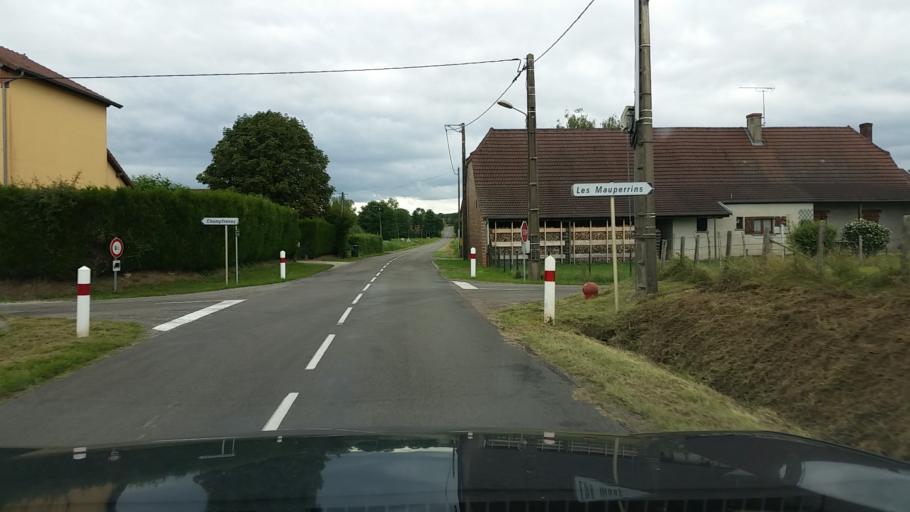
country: FR
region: Bourgogne
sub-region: Departement de Saone-et-Loire
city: Saint-Usuge
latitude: 46.7075
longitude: 5.3350
